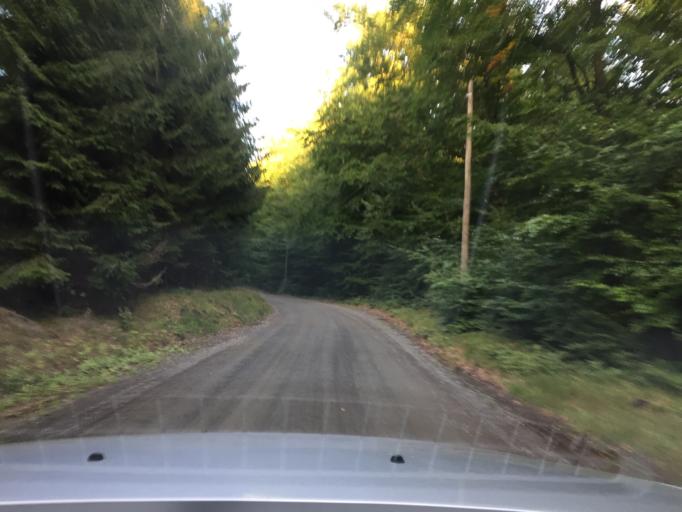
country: SE
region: Skane
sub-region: Hassleholms Kommun
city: Tormestorp
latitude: 56.0354
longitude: 13.7670
